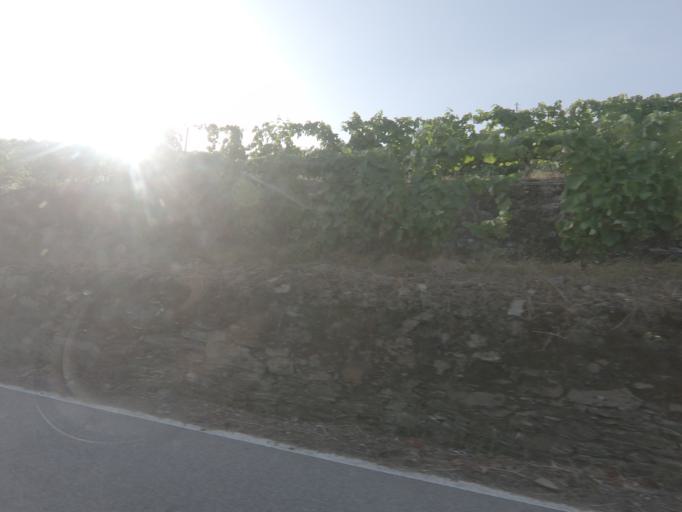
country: PT
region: Vila Real
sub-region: Sabrosa
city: Vilela
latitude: 41.2043
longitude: -7.5322
